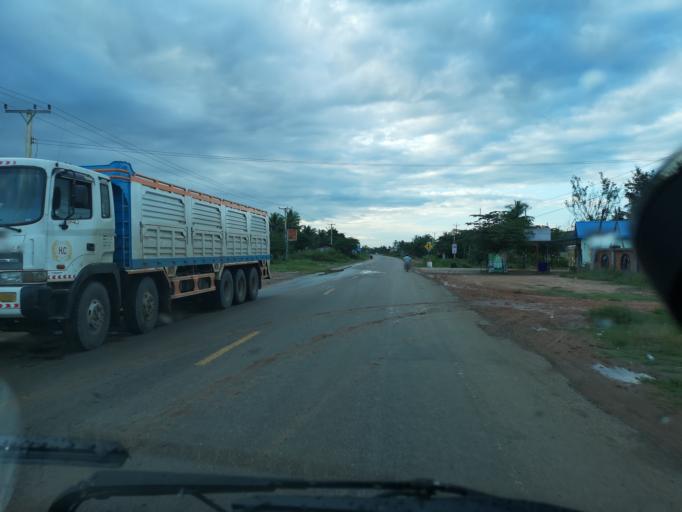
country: KH
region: Otar Meanchey
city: Samraong
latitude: 14.1643
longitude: 103.5180
